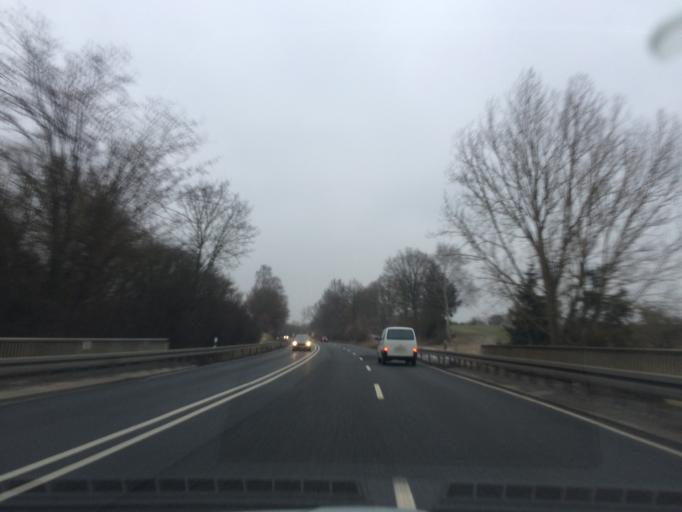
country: DE
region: Hesse
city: Grebenstein
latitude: 51.4384
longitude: 9.4114
